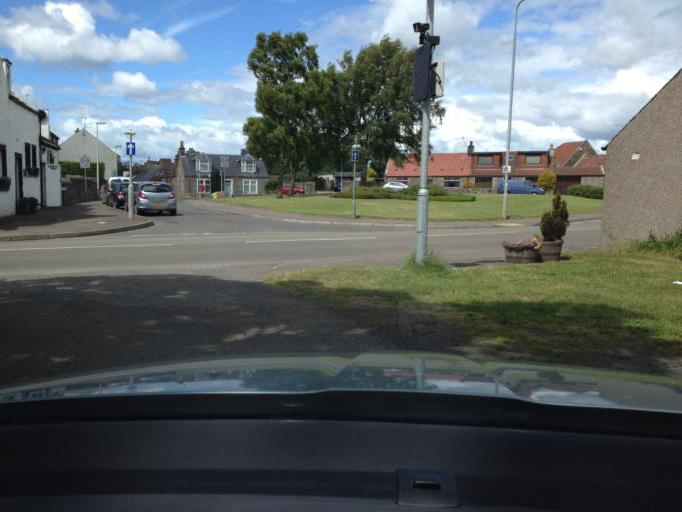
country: GB
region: Scotland
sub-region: Fife
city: Ladybank
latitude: 56.2737
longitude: -3.0739
